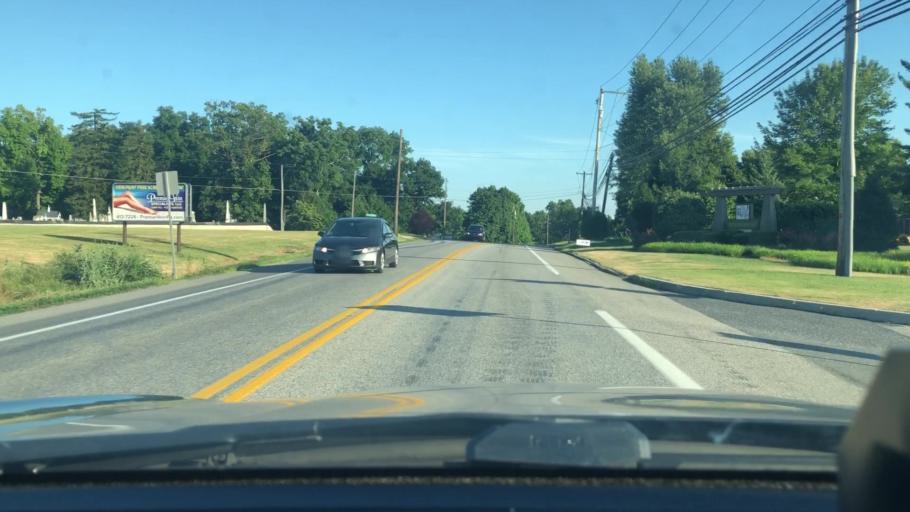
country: US
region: Pennsylvania
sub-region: Cumberland County
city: Mechanicsburg
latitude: 40.2398
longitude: -77.0082
